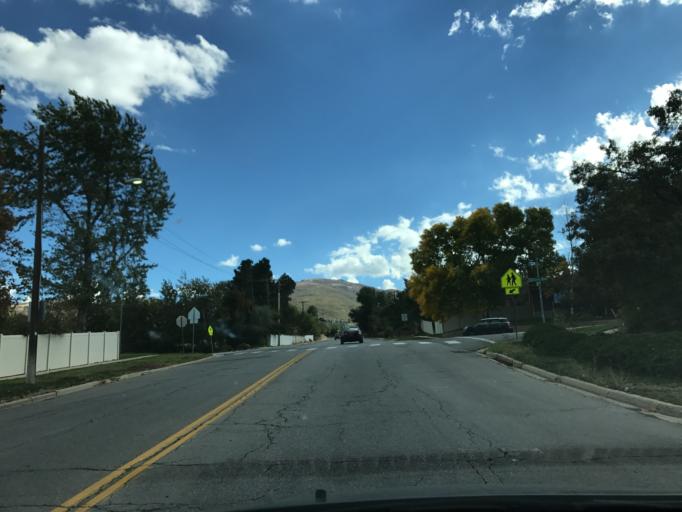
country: US
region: Utah
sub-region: Davis County
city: Bountiful
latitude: 40.8711
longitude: -111.8682
